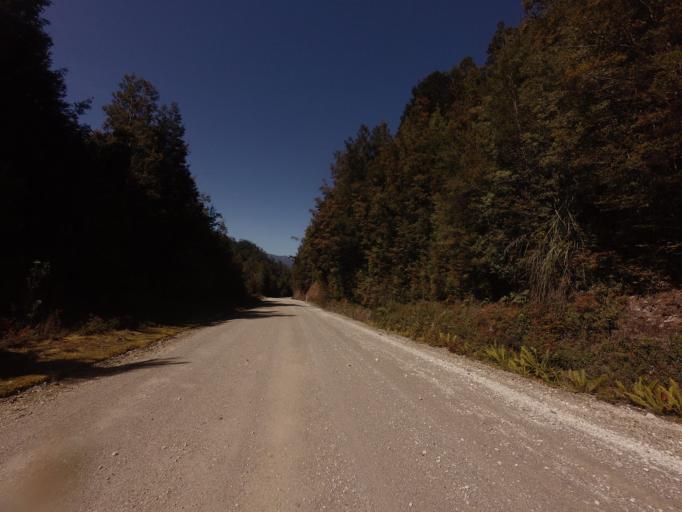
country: AU
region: Tasmania
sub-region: Huon Valley
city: Geeveston
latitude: -42.8416
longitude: 146.3758
